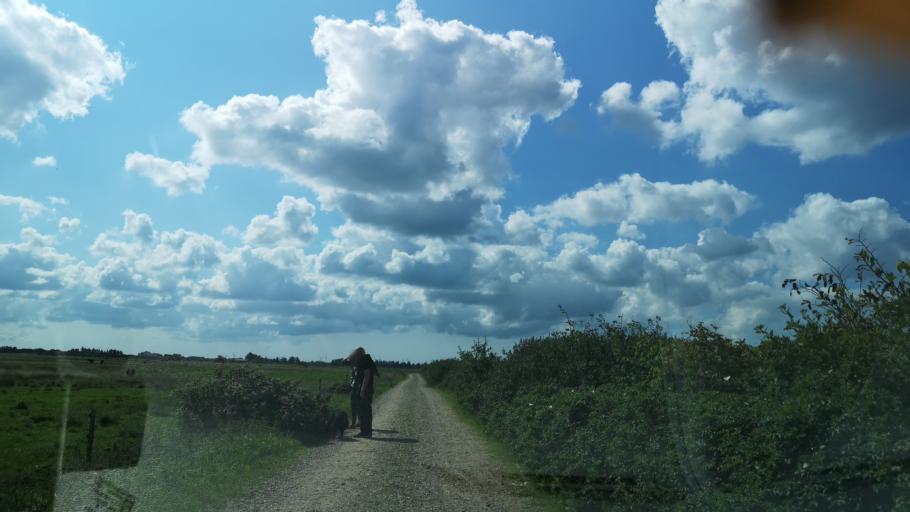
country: DK
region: Central Jutland
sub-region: Ringkobing-Skjern Kommune
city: Skjern
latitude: 55.9127
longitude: 8.4048
